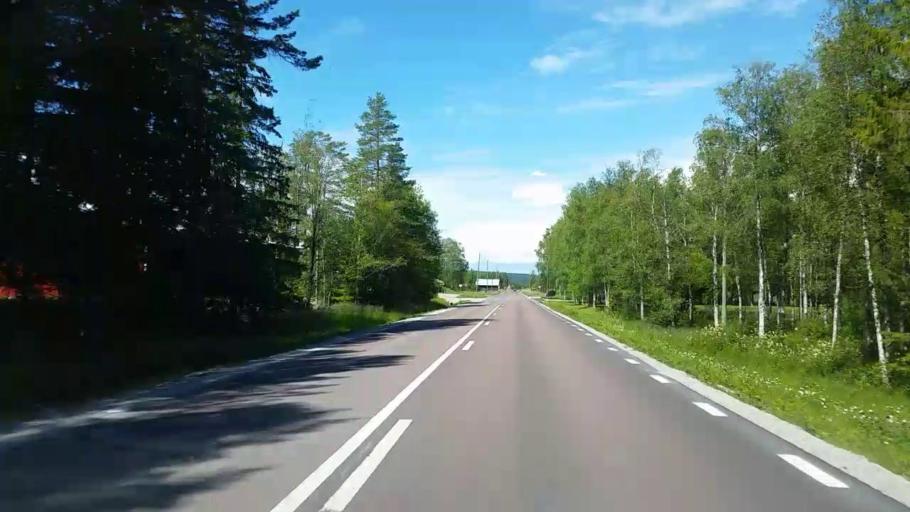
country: SE
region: Dalarna
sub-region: Rattviks Kommun
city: Raettvik
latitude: 61.0362
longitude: 15.2016
